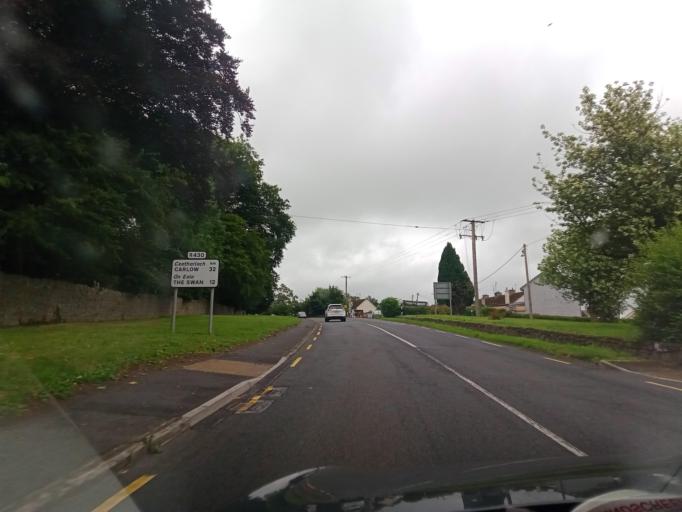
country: IE
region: Leinster
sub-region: Laois
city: Abbeyleix
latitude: 52.9110
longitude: -7.3370
